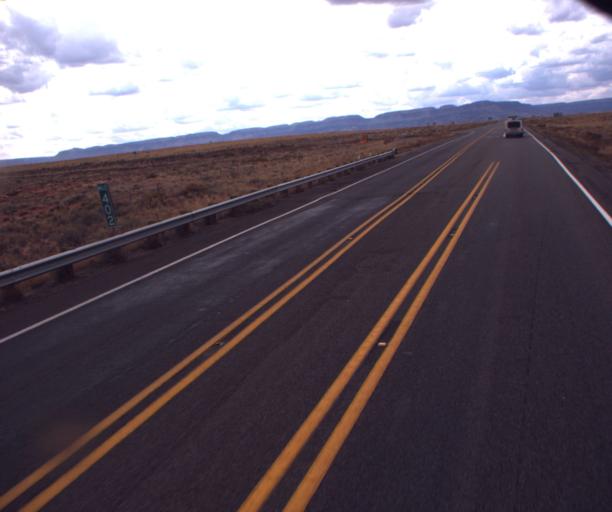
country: US
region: Arizona
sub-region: Navajo County
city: Kayenta
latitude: 36.7329
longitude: -110.0983
